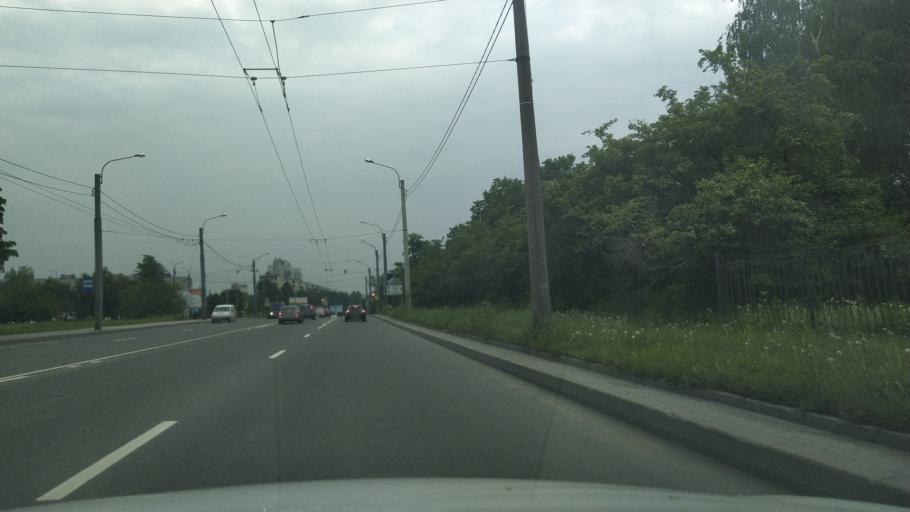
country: RU
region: St.-Petersburg
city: Kupchino
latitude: 59.8752
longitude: 30.3549
